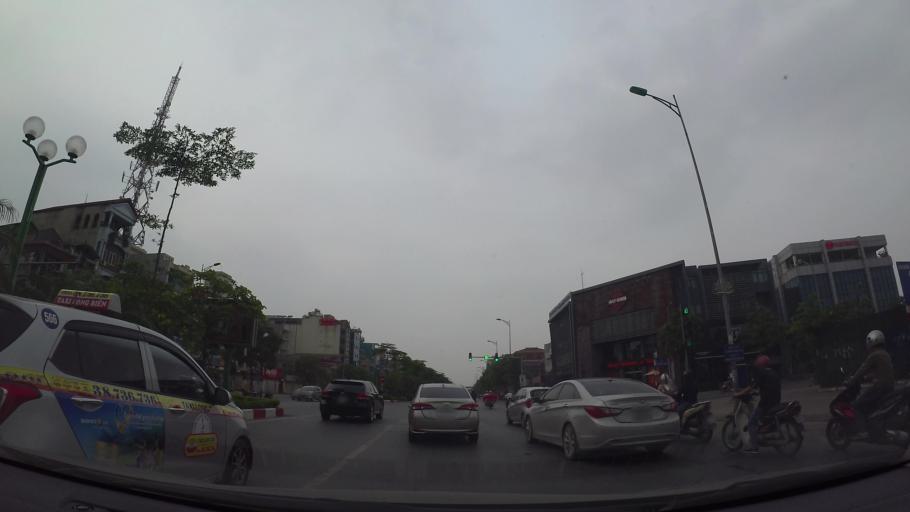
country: VN
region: Ha Noi
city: Hoan Kiem
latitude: 21.0573
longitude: 105.8901
